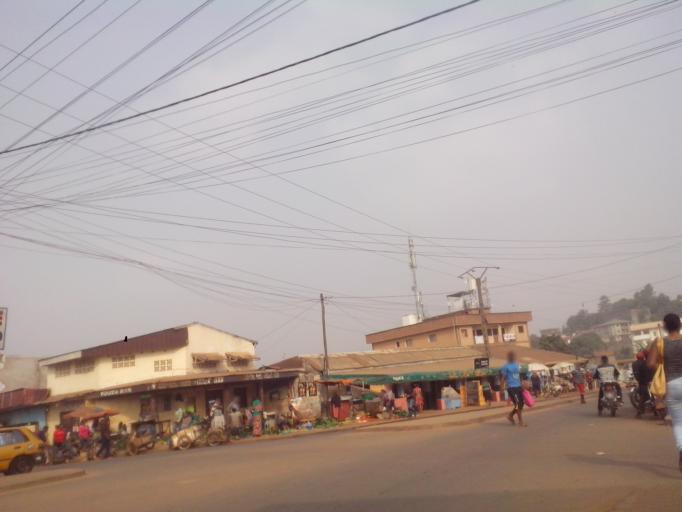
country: CM
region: Centre
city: Yaounde
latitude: 3.8502
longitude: 11.4936
